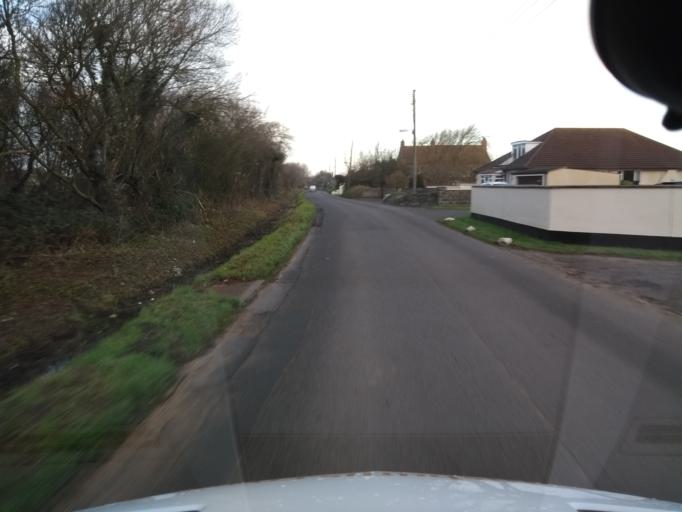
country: GB
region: England
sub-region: Somerset
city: Burnham-on-Sea
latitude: 51.2696
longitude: -3.0121
